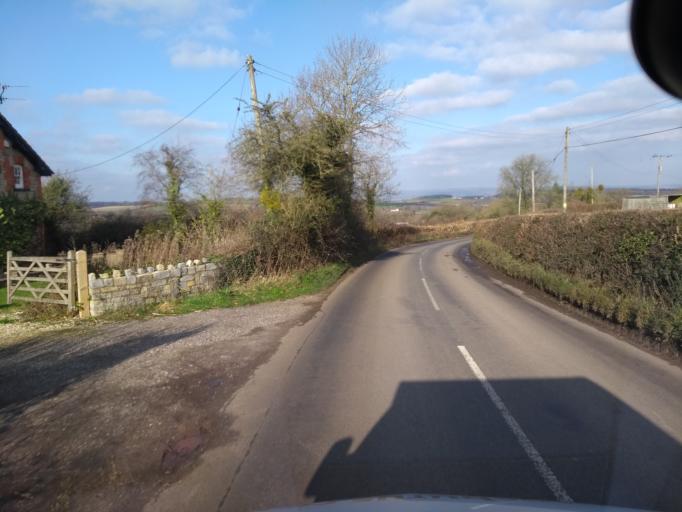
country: GB
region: England
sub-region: Somerset
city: Creech Saint Michael
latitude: 50.9461
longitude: -3.0412
